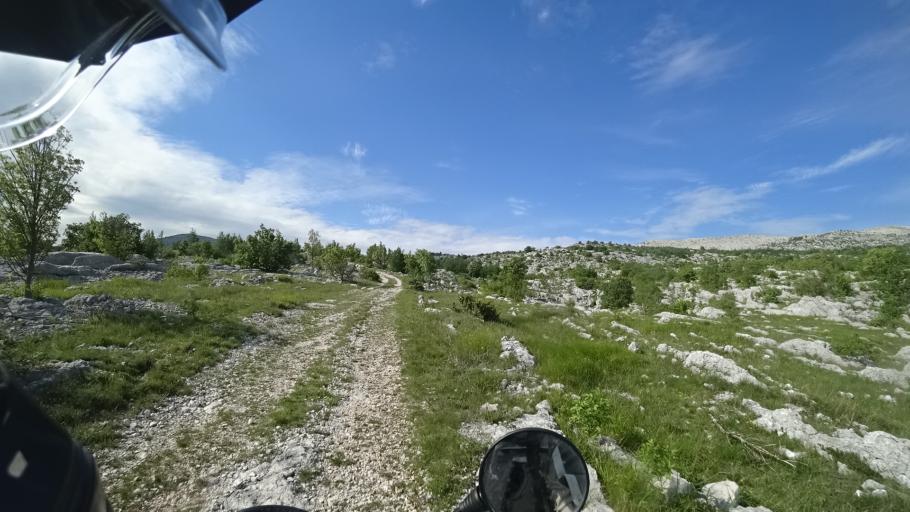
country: HR
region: Splitsko-Dalmatinska
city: Hrvace
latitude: 43.7916
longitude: 16.4346
